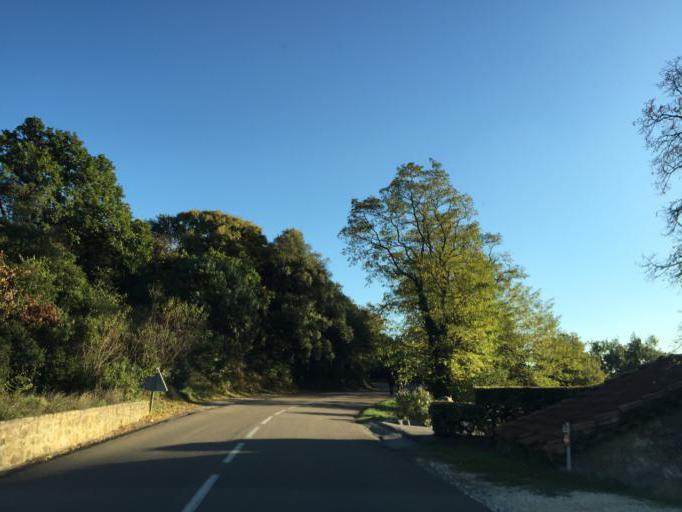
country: FR
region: Rhone-Alpes
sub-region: Departement de l'Ardeche
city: Bourg-Saint-Andeol
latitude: 44.4385
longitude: 4.6260
